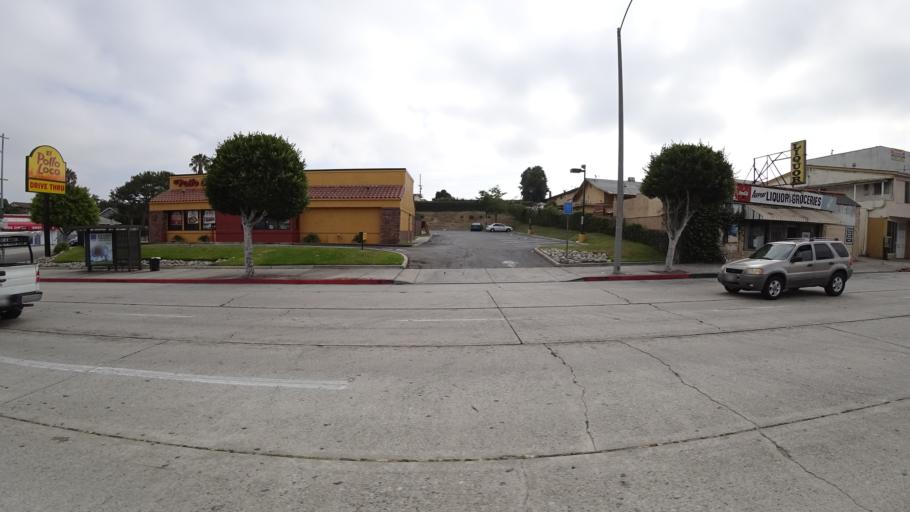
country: US
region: California
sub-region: Los Angeles County
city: Inglewood
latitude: 33.9687
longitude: -118.3555
